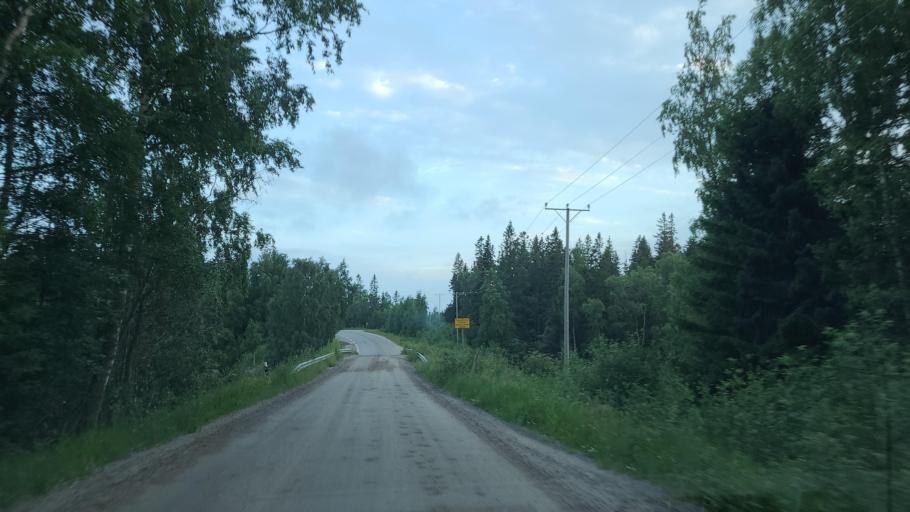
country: FI
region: Ostrobothnia
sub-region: Vaasa
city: Replot
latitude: 63.2939
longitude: 21.1111
